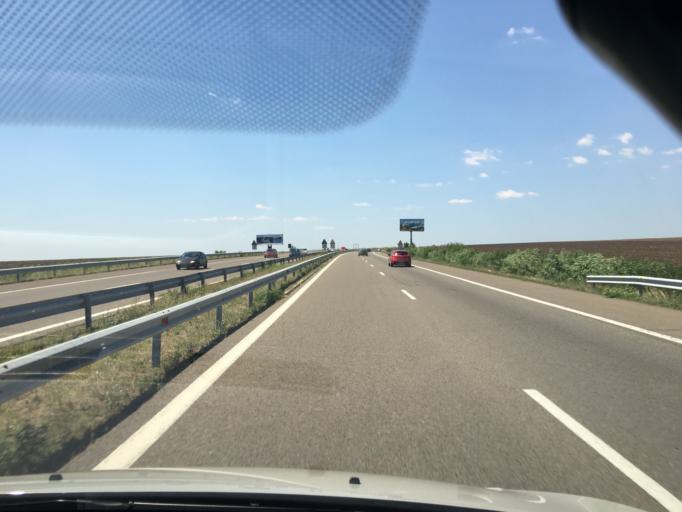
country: BG
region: Burgas
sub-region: Obshtina Kameno
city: Kameno
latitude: 42.5866
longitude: 27.1993
